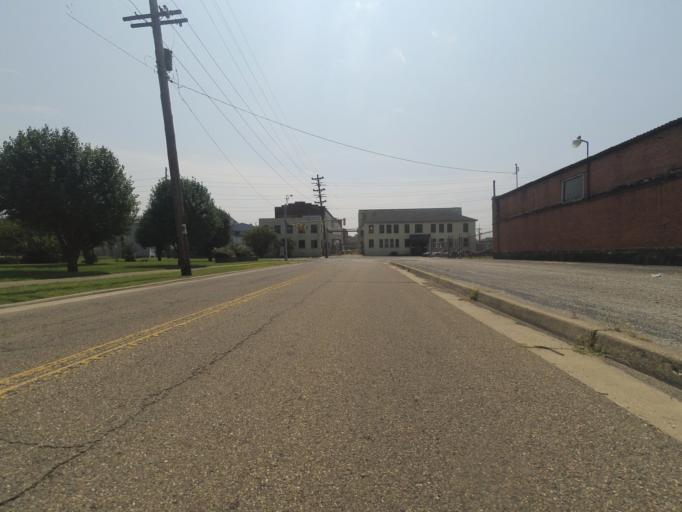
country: US
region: West Virginia
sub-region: Cabell County
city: Huntington
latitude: 38.4247
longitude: -82.4158
